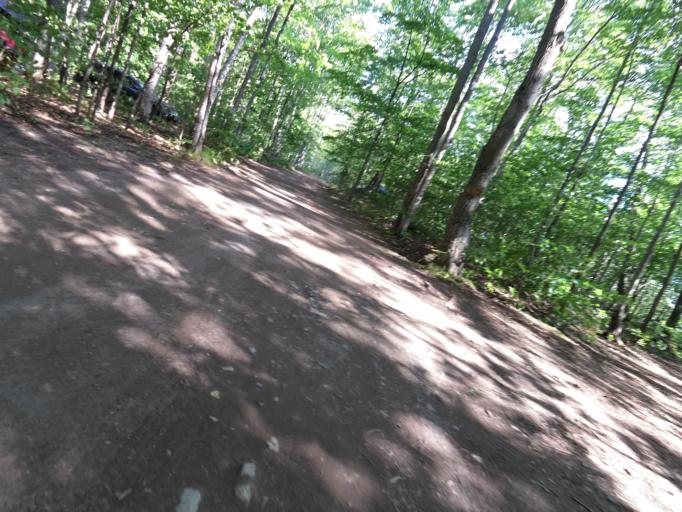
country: CA
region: Ontario
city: Tobermory
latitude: 45.2290
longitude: -81.6470
